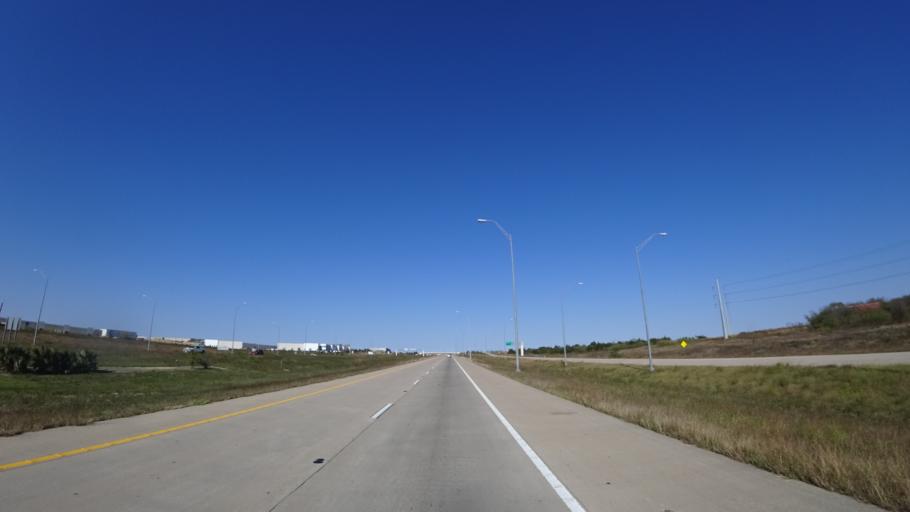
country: US
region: Texas
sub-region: Travis County
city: Pflugerville
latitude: 30.4151
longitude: -97.5855
